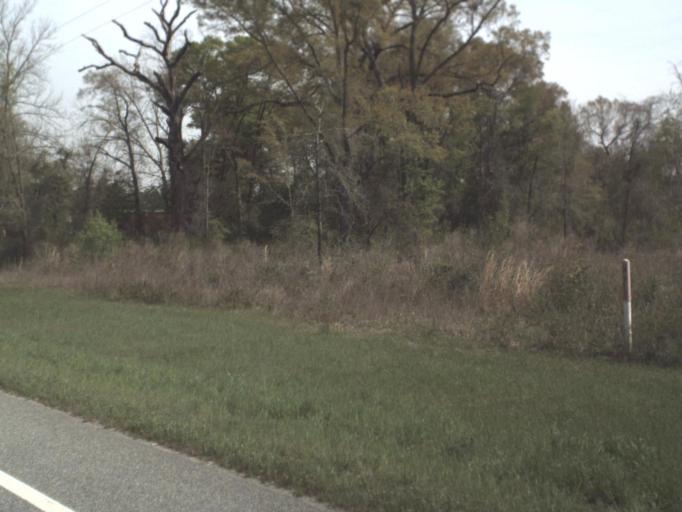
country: US
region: Florida
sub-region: Jackson County
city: Malone
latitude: 30.9750
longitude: -85.0899
